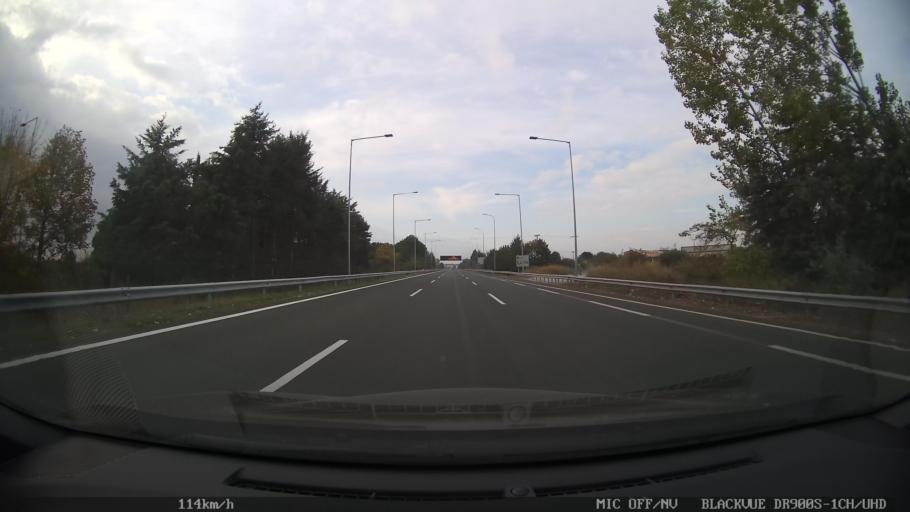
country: GR
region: Central Macedonia
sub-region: Nomos Pierias
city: Peristasi
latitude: 40.2854
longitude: 22.5286
